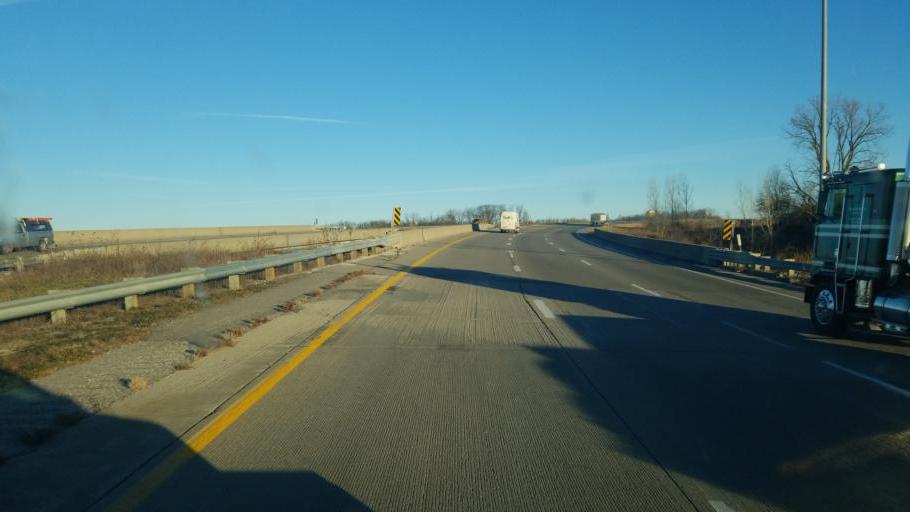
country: US
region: Iowa
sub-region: Wapello County
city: Eddyville
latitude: 41.1504
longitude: -92.6237
